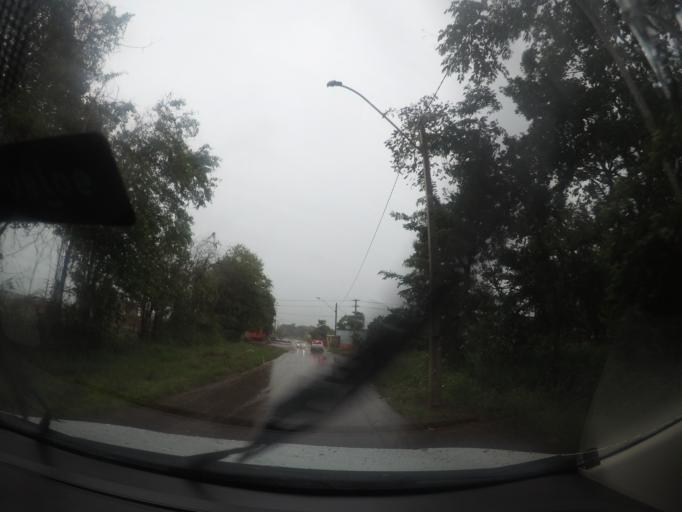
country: BR
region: Goias
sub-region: Goiania
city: Goiania
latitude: -16.5904
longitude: -49.3227
